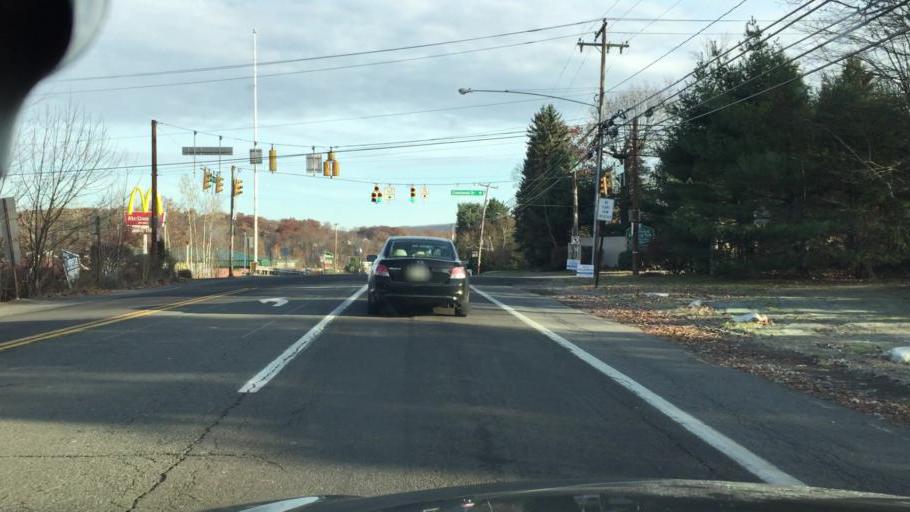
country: US
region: Pennsylvania
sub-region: Luzerne County
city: Mountain Top
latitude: 41.1432
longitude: -75.8999
